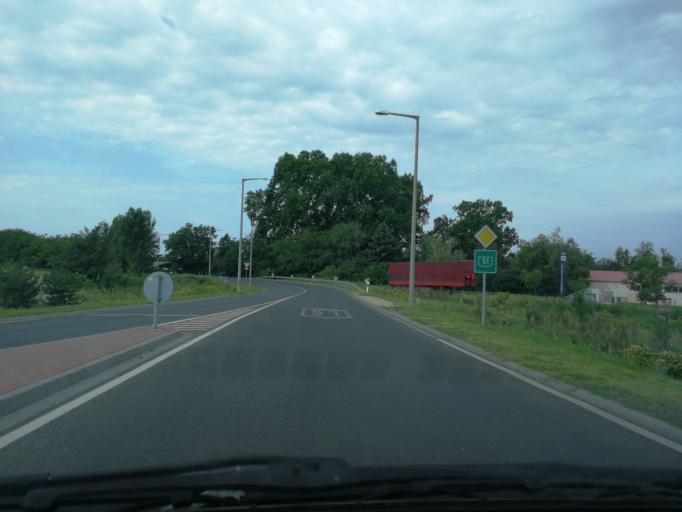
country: HU
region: Bacs-Kiskun
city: Baja
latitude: 46.2157
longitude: 18.9619
